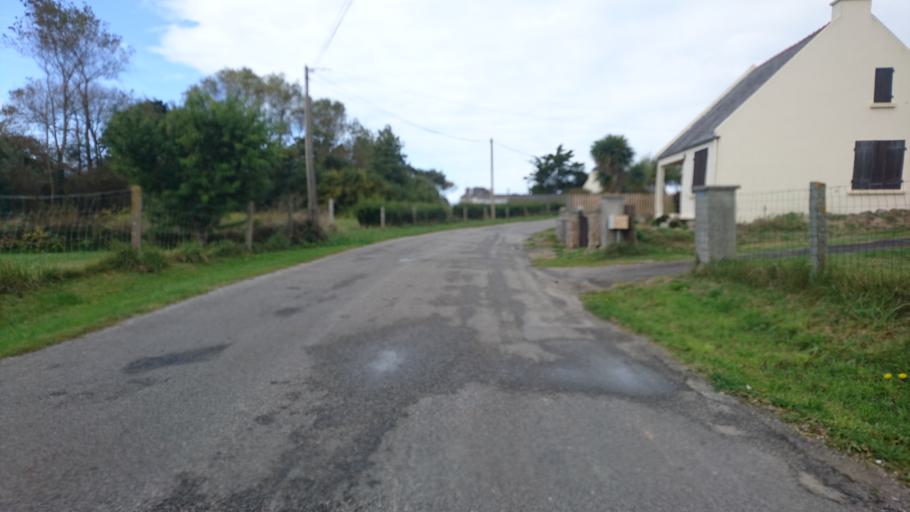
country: FR
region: Brittany
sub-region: Departement du Finistere
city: Lampaul-Plouarzel
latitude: 48.4440
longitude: -4.7728
